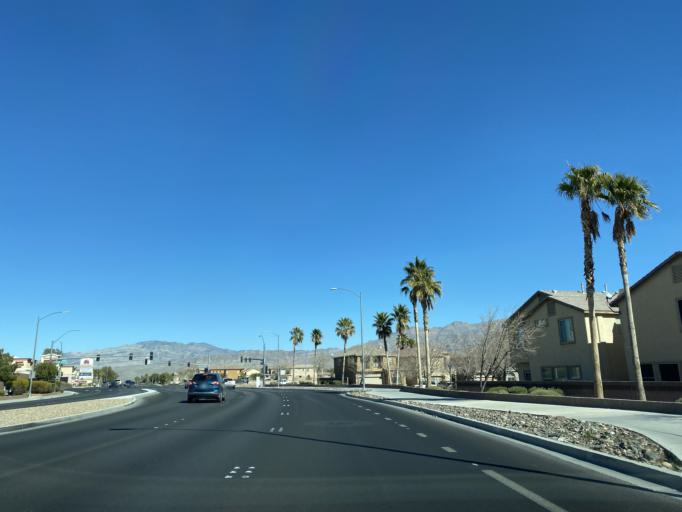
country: US
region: Nevada
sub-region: Clark County
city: Las Vegas
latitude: 36.3052
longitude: -115.2789
